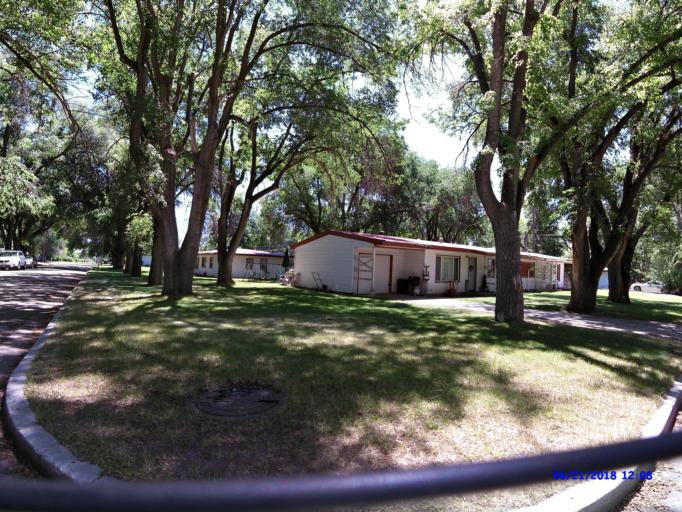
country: US
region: Utah
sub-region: Weber County
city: Harrisville
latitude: 41.2852
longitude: -112.0056
